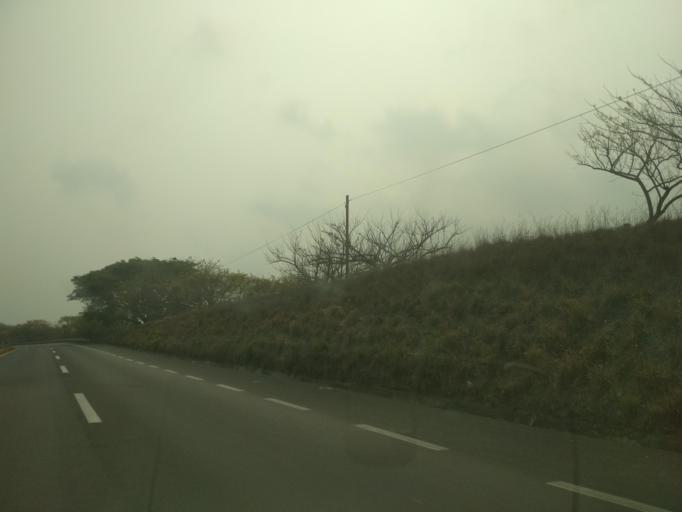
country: MX
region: Veracruz
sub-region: Veracruz
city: Delfino Victoria (Santa Fe)
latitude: 19.2246
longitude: -96.2570
